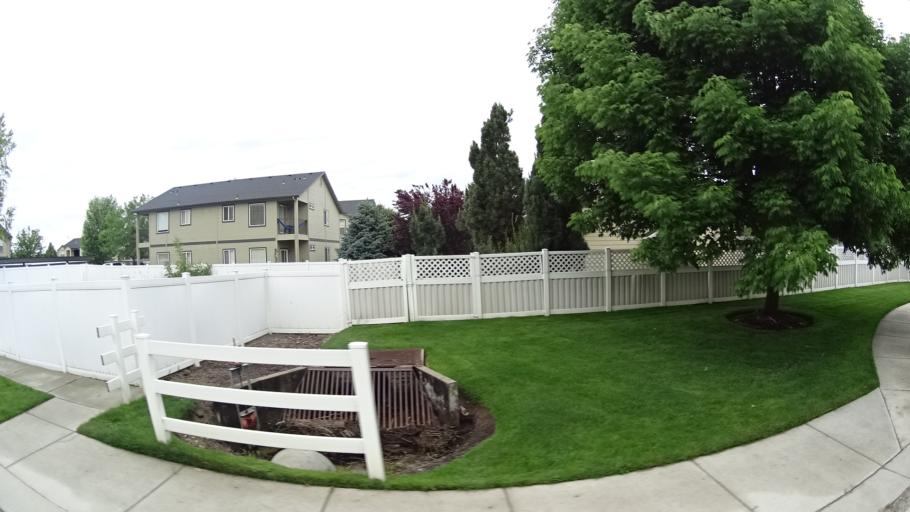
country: US
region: Idaho
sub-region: Ada County
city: Star
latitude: 43.6939
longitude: -116.4733
